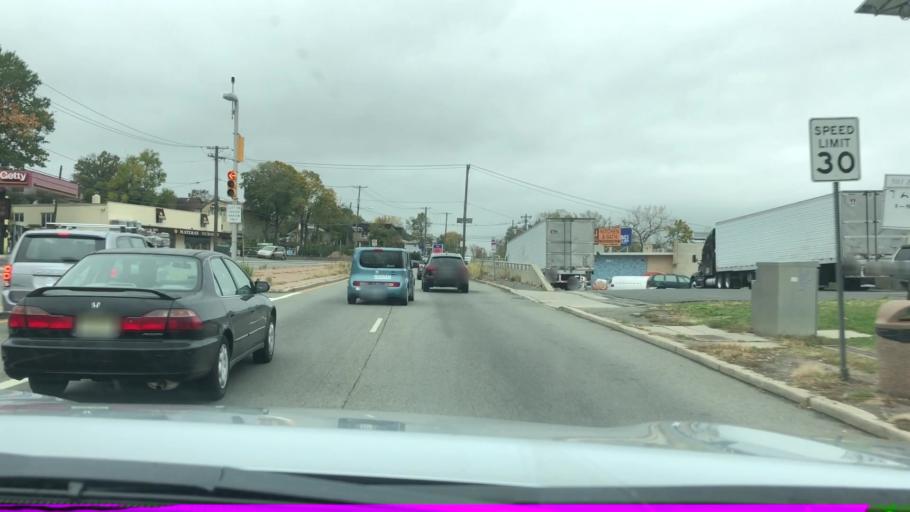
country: US
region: New Jersey
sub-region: Bergen County
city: Ridgefield
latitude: 40.8322
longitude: -74.0103
